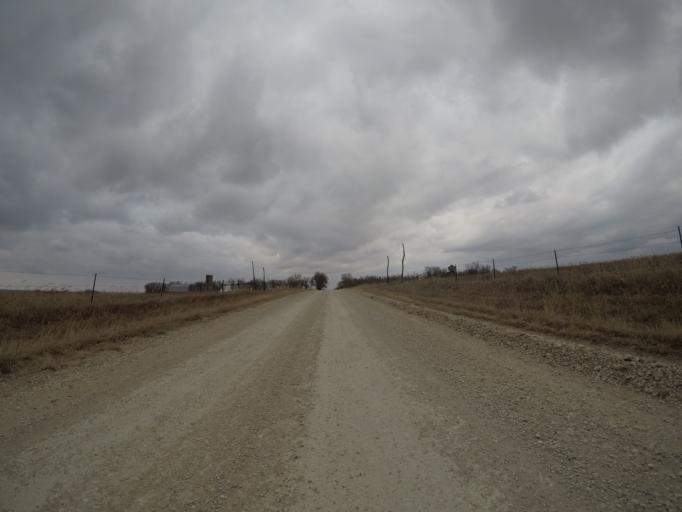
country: US
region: Kansas
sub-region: Morris County
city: Council Grove
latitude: 38.7423
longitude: -96.2796
